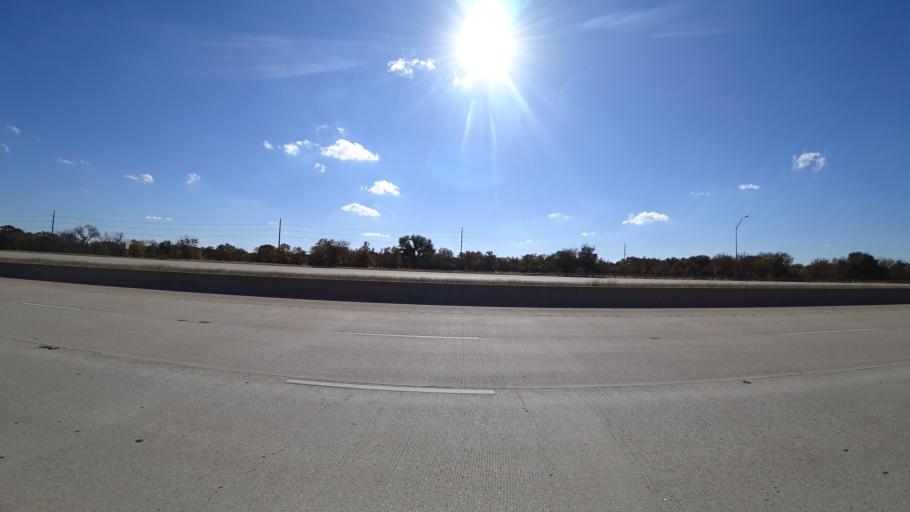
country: US
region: Texas
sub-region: Williamson County
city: Brushy Creek
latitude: 30.4785
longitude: -97.7316
